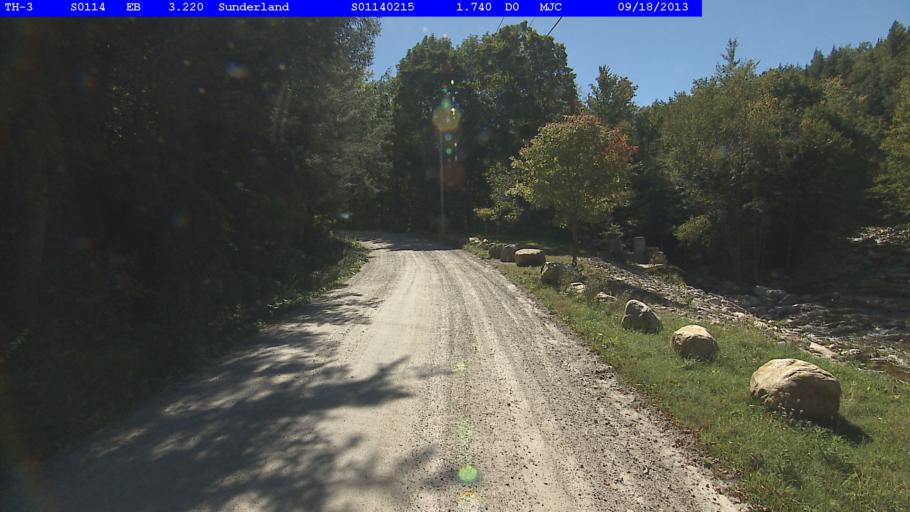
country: US
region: Vermont
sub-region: Bennington County
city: Arlington
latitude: 43.0485
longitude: -73.1162
